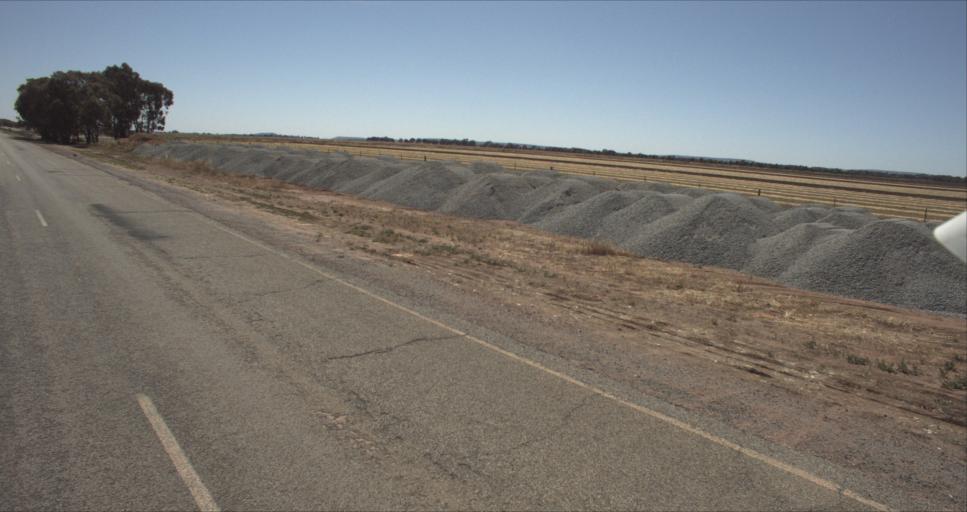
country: AU
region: New South Wales
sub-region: Leeton
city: Leeton
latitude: -34.4952
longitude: 146.2880
